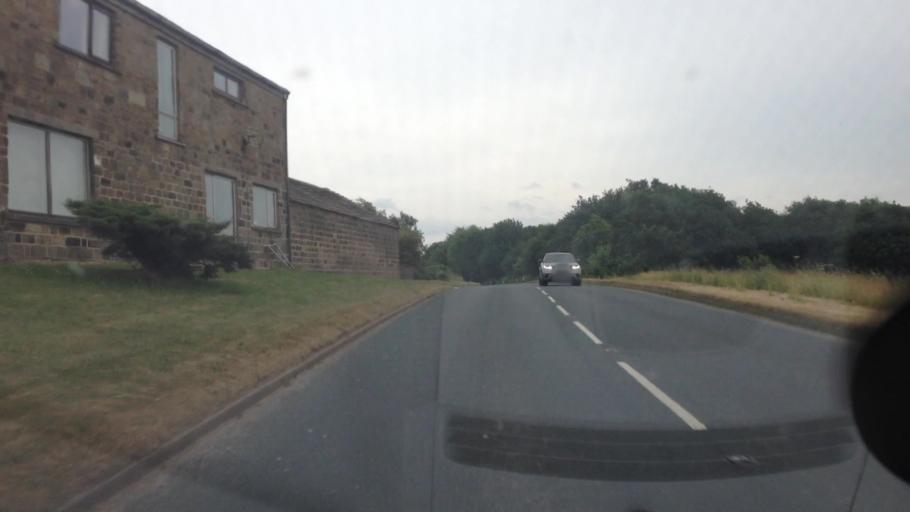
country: GB
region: England
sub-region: City and Borough of Wakefield
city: Woolley
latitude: 53.6132
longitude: -1.5353
